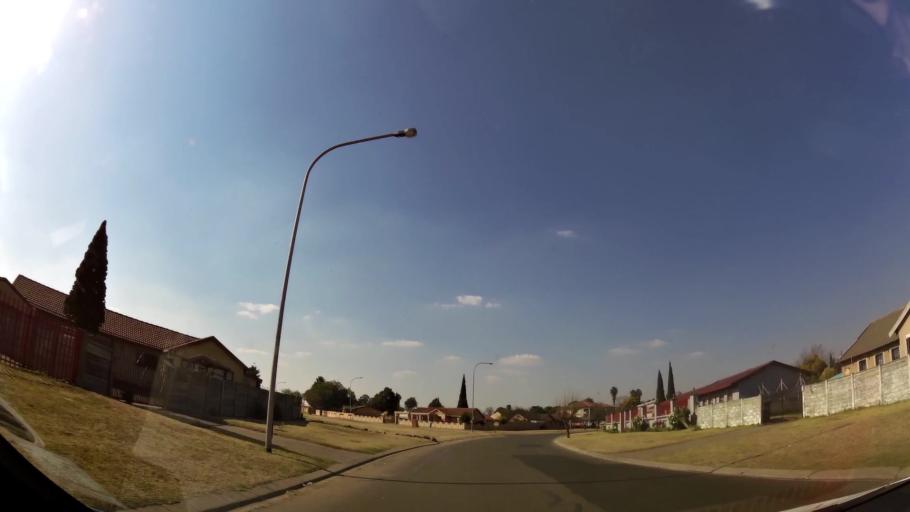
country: ZA
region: Gauteng
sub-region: Ekurhuleni Metropolitan Municipality
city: Benoni
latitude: -26.2394
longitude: 28.3091
